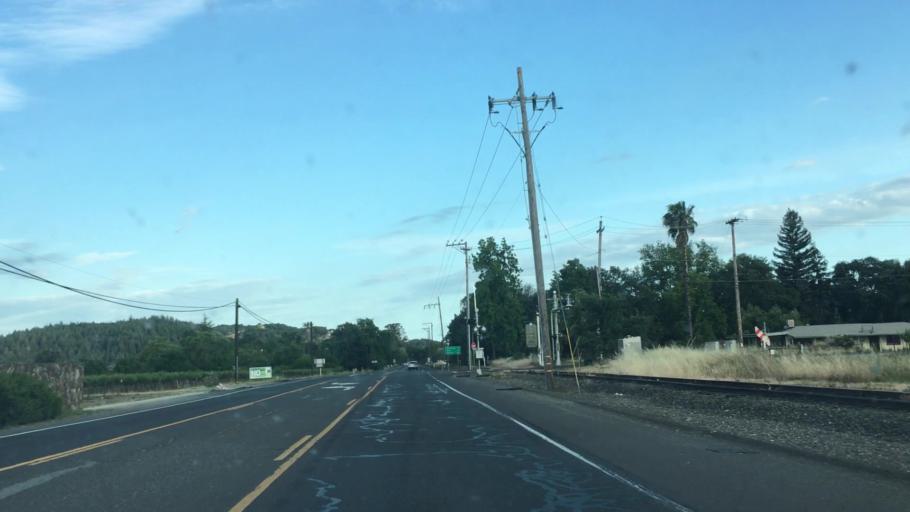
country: US
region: California
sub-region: Napa County
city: Yountville
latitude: 38.4348
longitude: -122.4010
